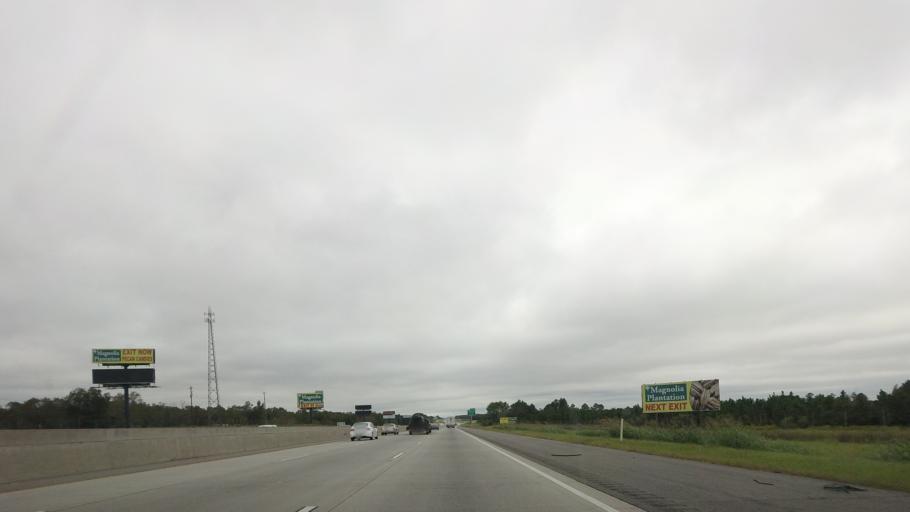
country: US
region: Georgia
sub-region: Tift County
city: Unionville
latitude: 31.3737
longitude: -83.4940
